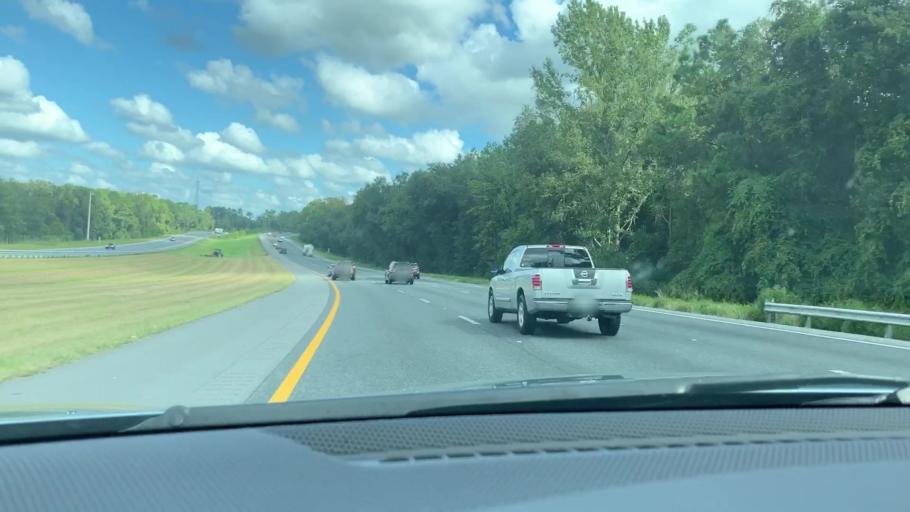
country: US
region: Florida
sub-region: Hernando County
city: Hill 'n Dale
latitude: 28.4545
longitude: -82.2750
